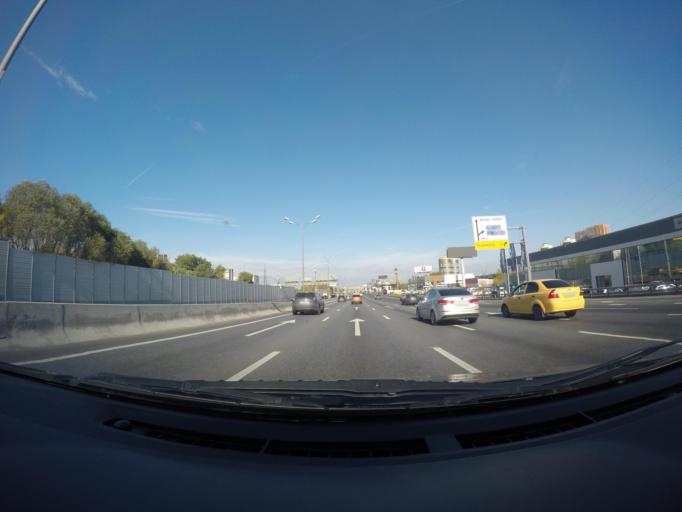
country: RU
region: Moscow
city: Ivanovskoye
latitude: 55.7522
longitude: 37.8424
